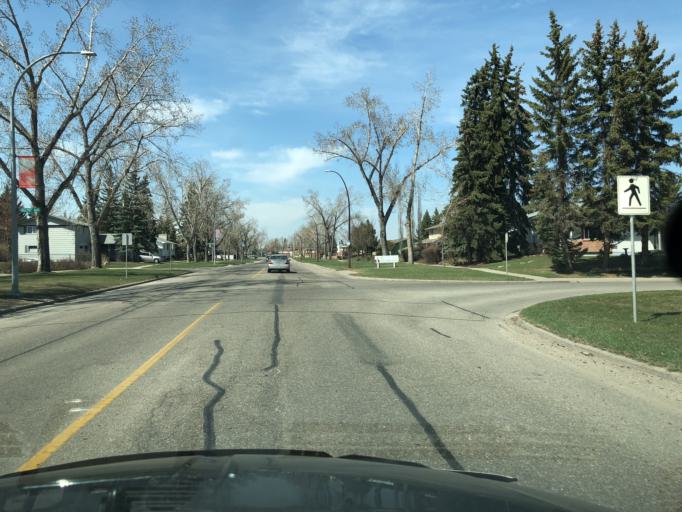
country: CA
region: Alberta
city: Calgary
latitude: 50.9577
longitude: -114.0418
